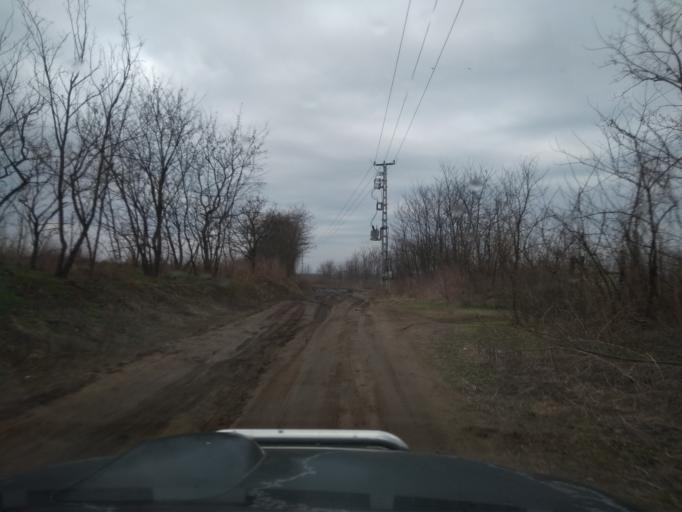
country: HU
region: Szabolcs-Szatmar-Bereg
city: Nyirpazony
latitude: 47.9993
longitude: 21.7889
